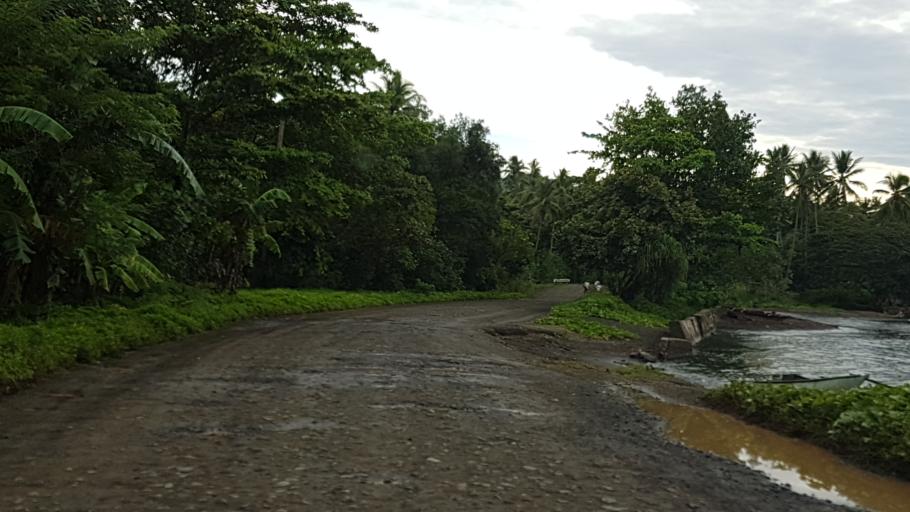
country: PG
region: Milne Bay
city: Alotau
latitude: -10.3342
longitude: 150.6489
